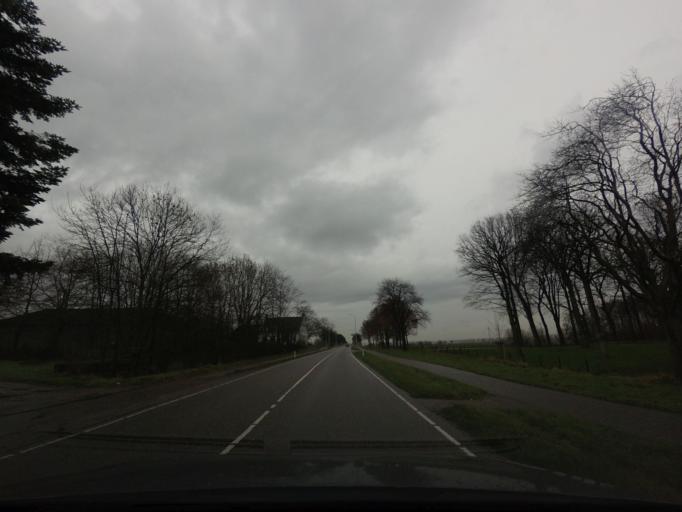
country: NL
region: North Brabant
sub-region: Gemeente Moerdijk
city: Klundert
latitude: 51.6286
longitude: 4.6297
